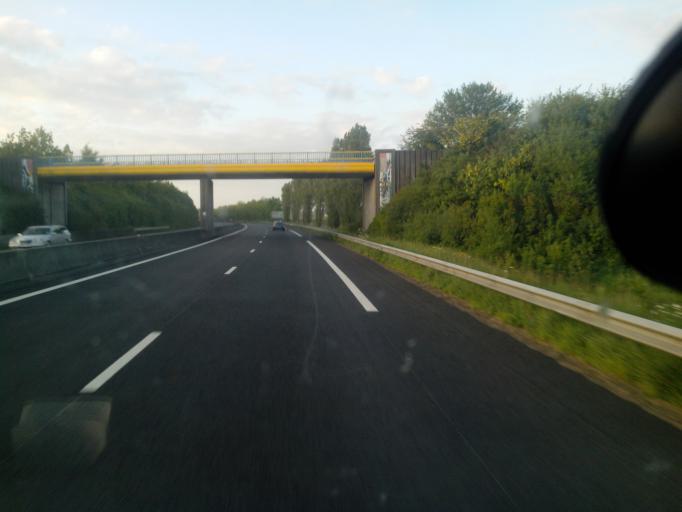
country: FR
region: Picardie
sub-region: Departement de la Somme
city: Bouttencourt
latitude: 49.9865
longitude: 1.6853
